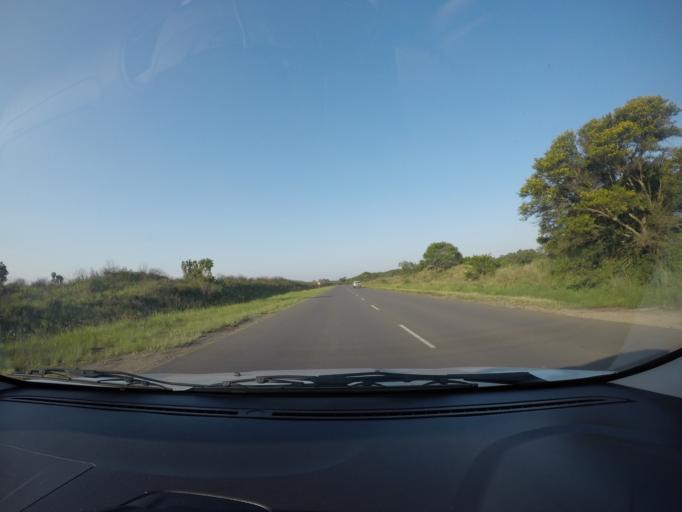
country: ZA
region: KwaZulu-Natal
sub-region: uThungulu District Municipality
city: Richards Bay
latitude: -28.7498
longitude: 32.0111
